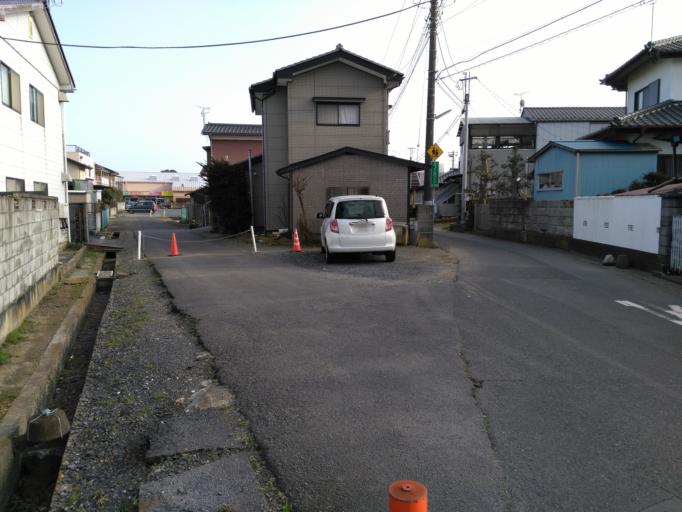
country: JP
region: Ibaraki
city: Oarai
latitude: 36.3168
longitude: 140.5664
